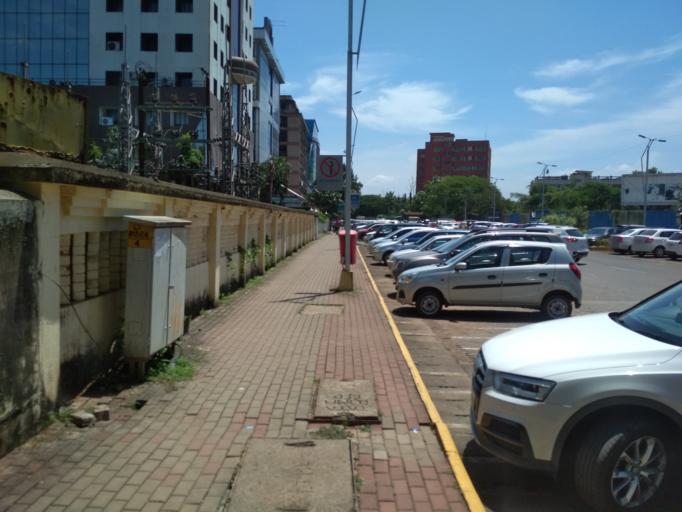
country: IN
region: Goa
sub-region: North Goa
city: Panaji
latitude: 15.4949
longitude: 73.8346
